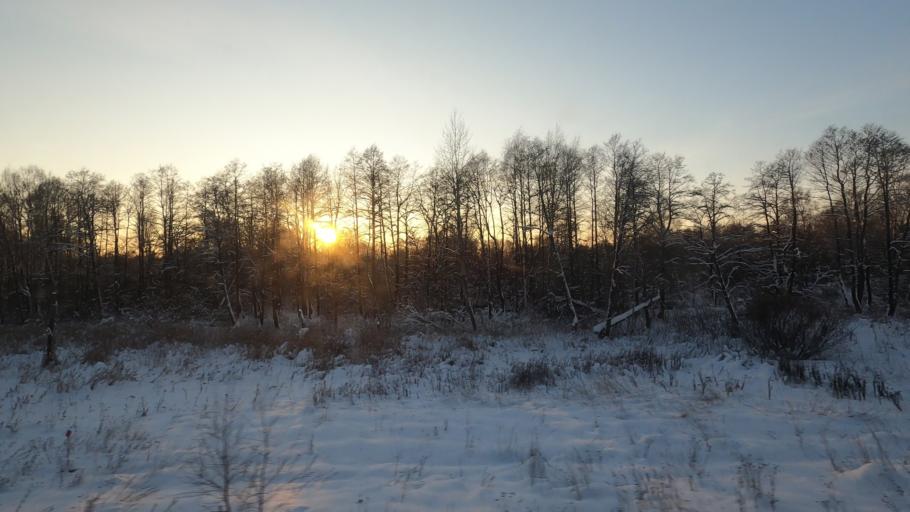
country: RU
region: Moskovskaya
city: Orud'yevo
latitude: 56.3950
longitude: 37.4981
